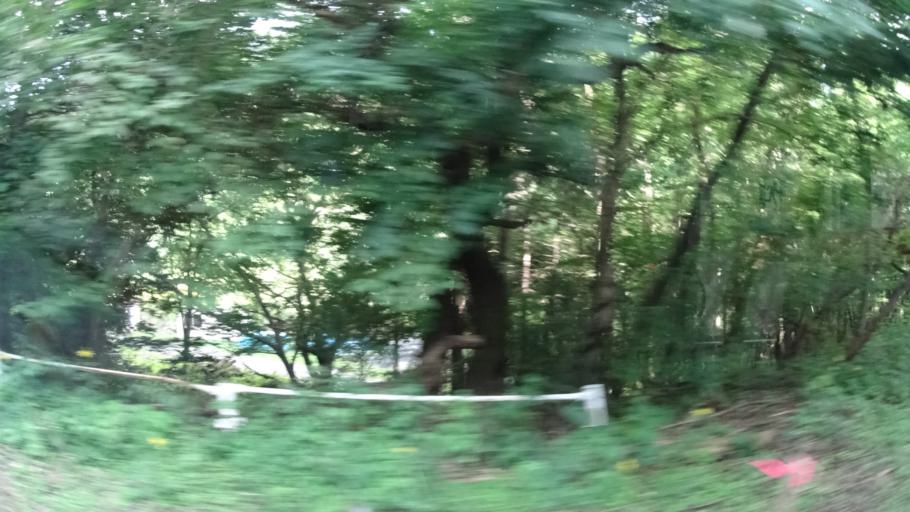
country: JP
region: Tochigi
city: Nikko
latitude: 36.6833
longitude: 139.4914
